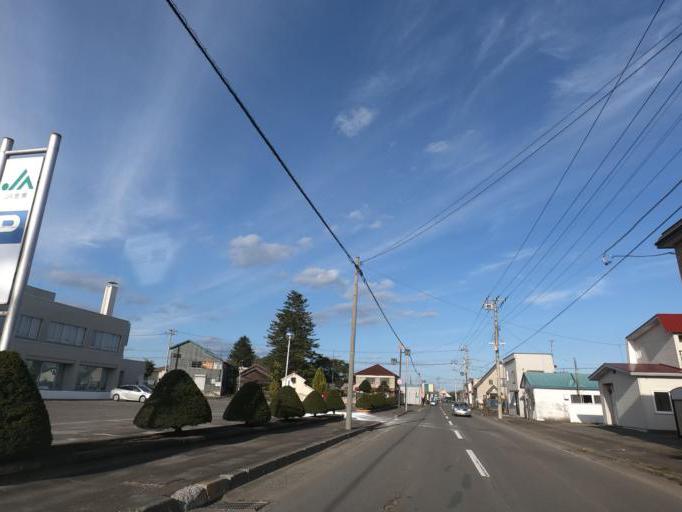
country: JP
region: Hokkaido
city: Obihiro
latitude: 42.5635
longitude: 143.3006
